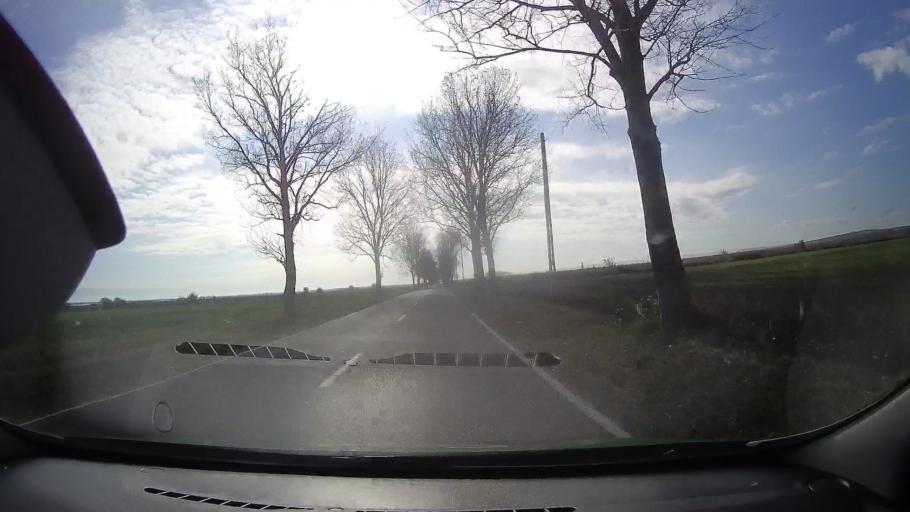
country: RO
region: Tulcea
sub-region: Comuna Valea Nucarilor
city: Agighiol
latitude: 45.0087
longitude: 28.8846
